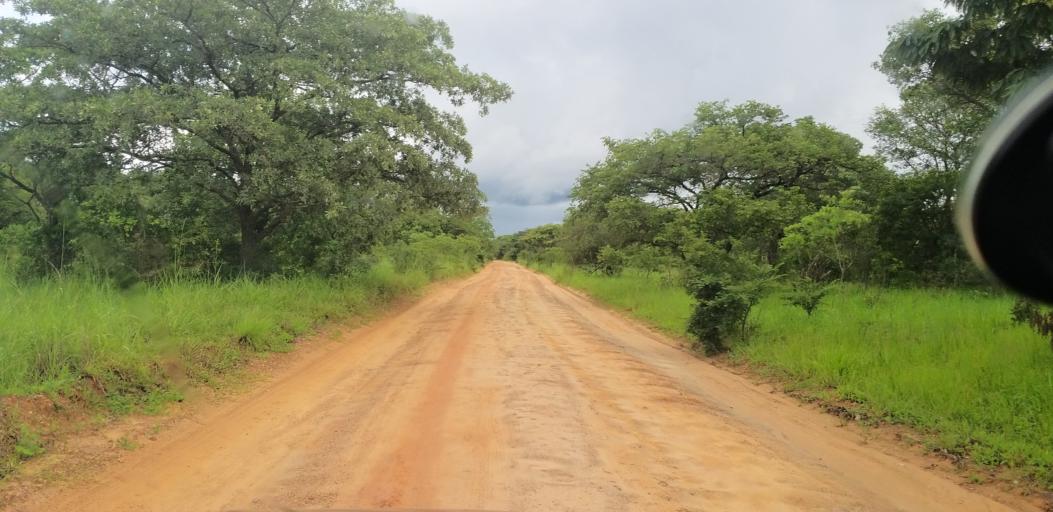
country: ZM
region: Lusaka
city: Chongwe
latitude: -15.1581
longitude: 28.4955
